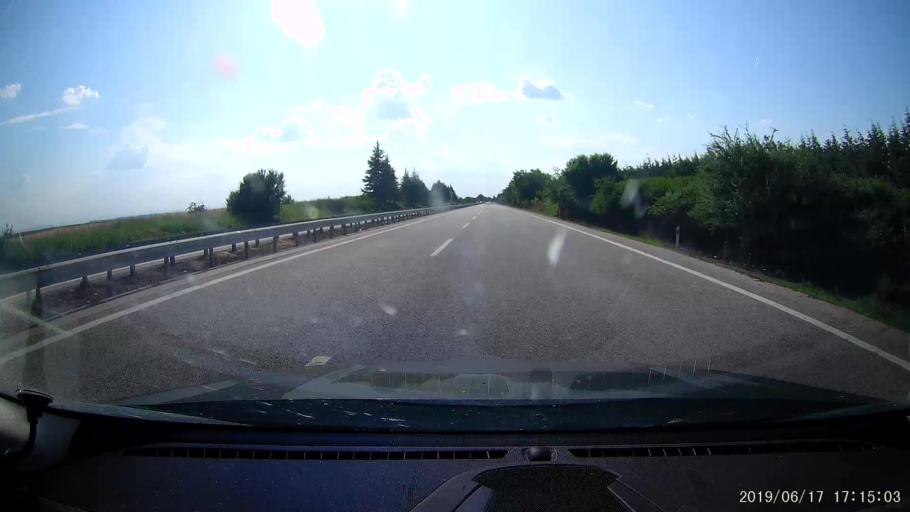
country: TR
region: Edirne
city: Edirne
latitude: 41.7005
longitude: 26.5051
